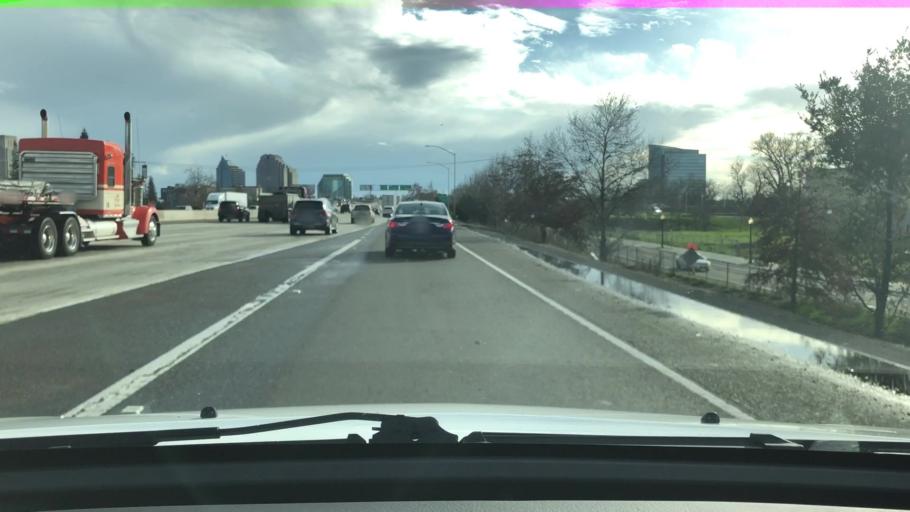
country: US
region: California
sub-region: Sacramento County
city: Sacramento
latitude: 38.5945
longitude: -121.5045
